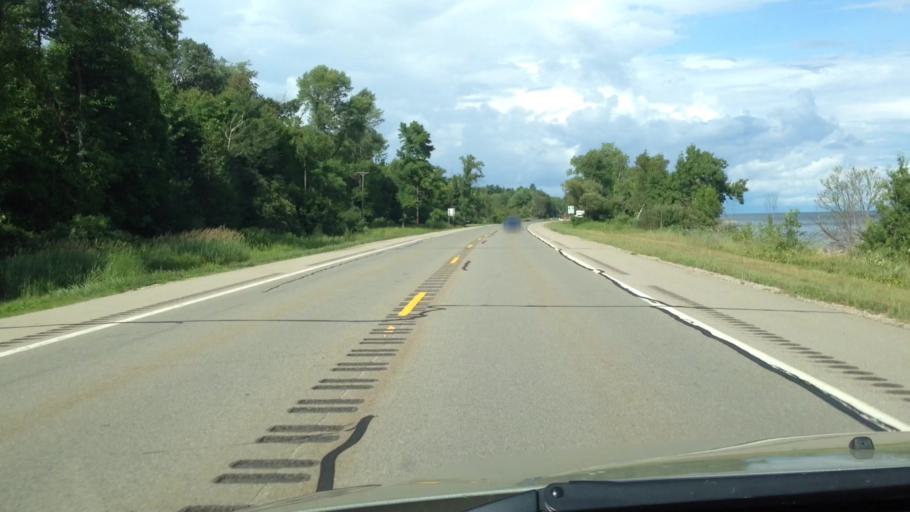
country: US
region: Michigan
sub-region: Menominee County
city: Menominee
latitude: 45.2526
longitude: -87.4856
